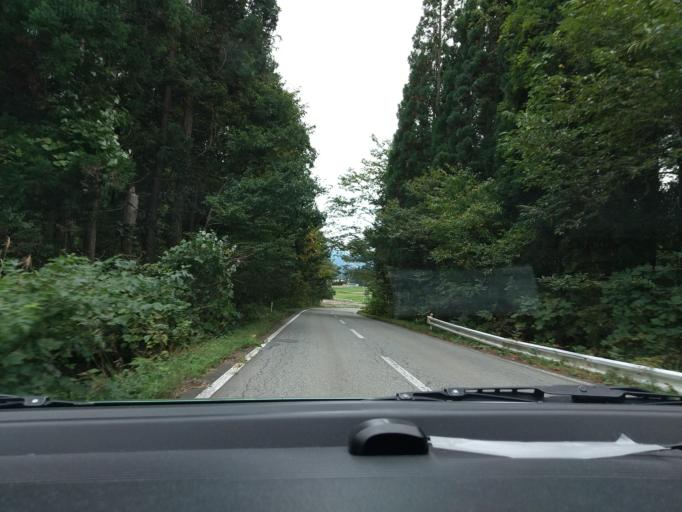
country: JP
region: Akita
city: Kakunodatemachi
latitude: 39.5483
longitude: 140.6338
